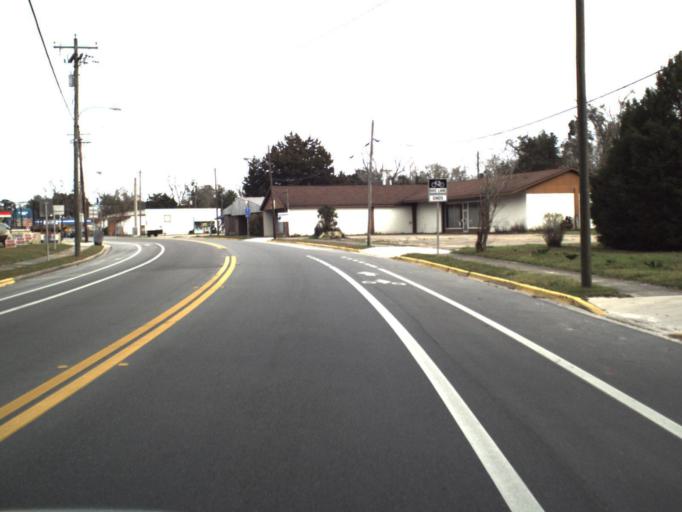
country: US
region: Florida
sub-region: Gulf County
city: Wewahitchka
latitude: 30.1131
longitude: -85.2021
